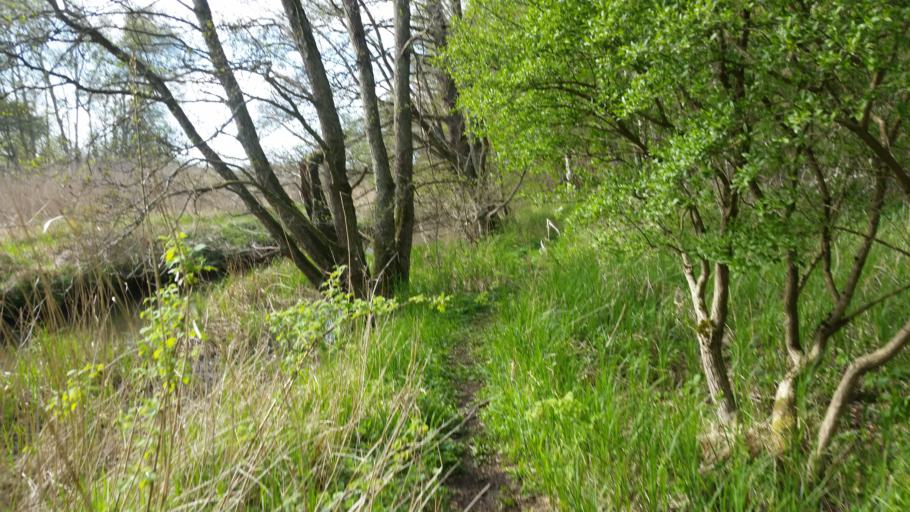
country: DK
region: Capital Region
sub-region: Gribskov Kommune
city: Gilleleje
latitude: 56.0655
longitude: 12.3658
